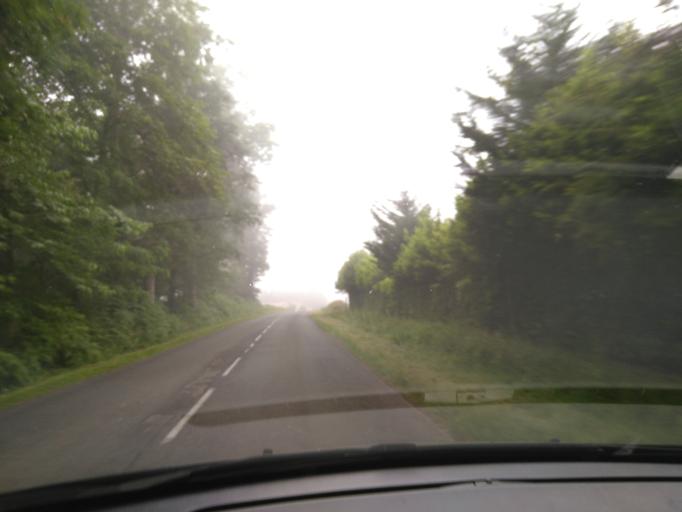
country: FR
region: Midi-Pyrenees
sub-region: Departement du Gers
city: Le Houga
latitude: 43.8619
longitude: -0.2132
